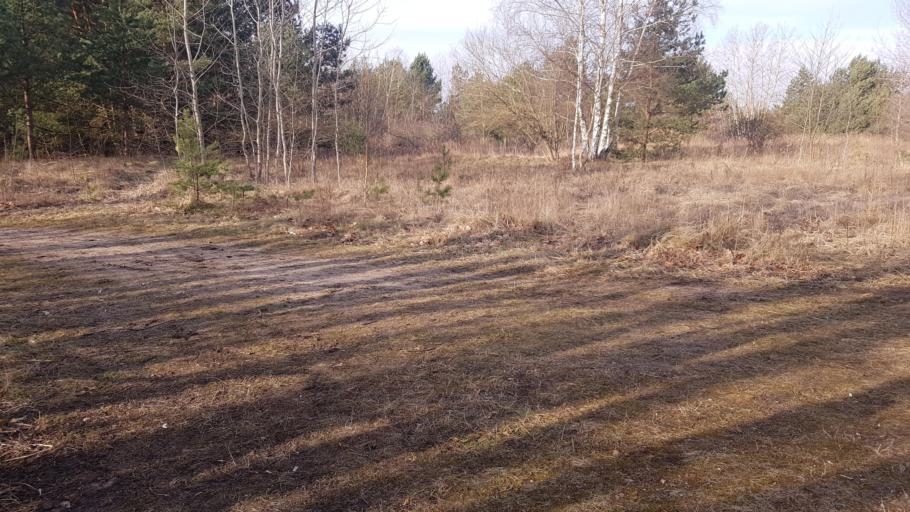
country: DE
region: Brandenburg
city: Stahnsdorf
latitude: 52.3545
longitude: 13.1795
